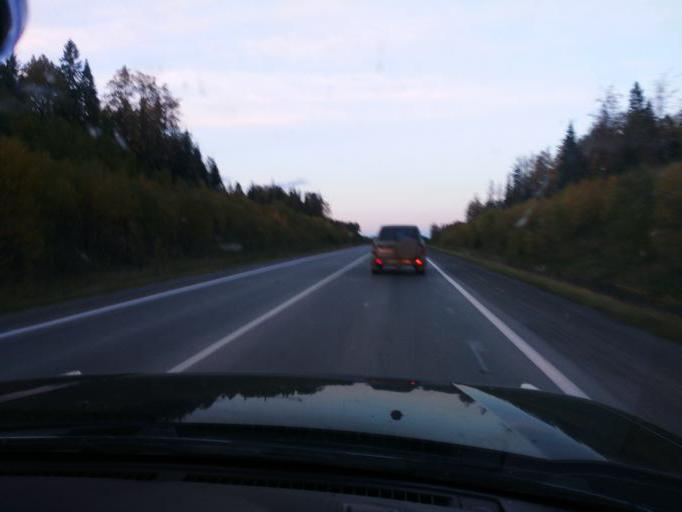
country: RU
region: Perm
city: Sylva
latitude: 58.2878
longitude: 56.7431
